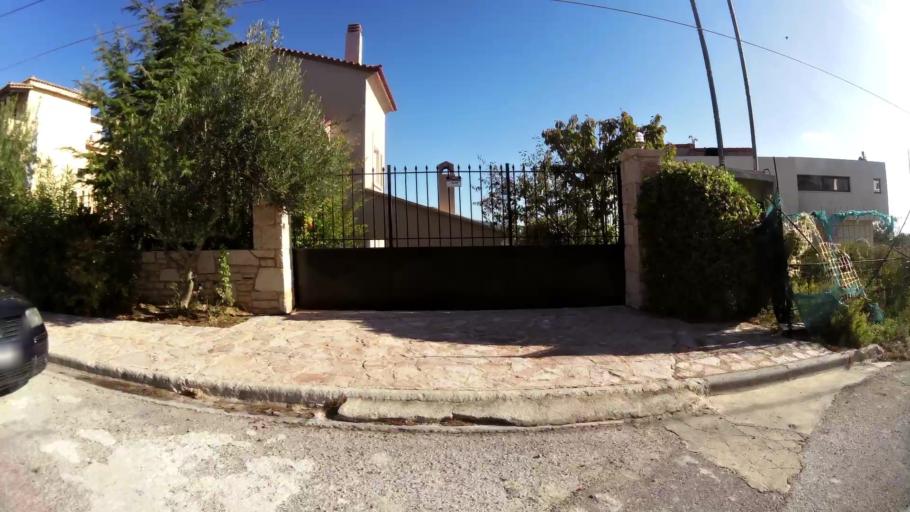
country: GR
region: Attica
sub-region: Nomarchia Anatolikis Attikis
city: Dhrafi
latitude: 38.0243
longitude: 23.9045
